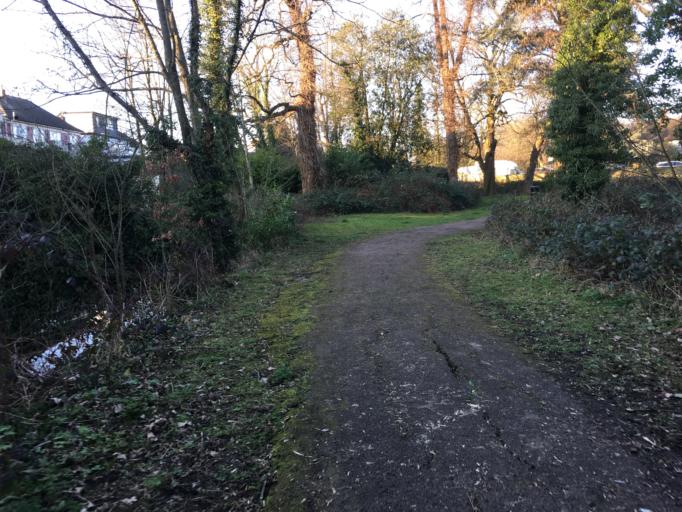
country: GB
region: England
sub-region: Greater London
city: Hendon
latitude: 51.5862
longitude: -0.2114
